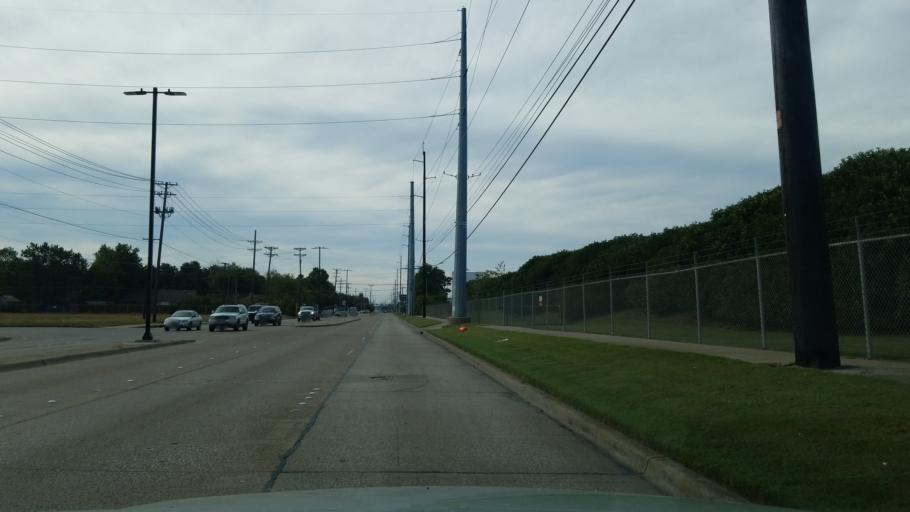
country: US
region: Texas
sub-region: Dallas County
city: Garland
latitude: 32.9056
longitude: -96.6656
